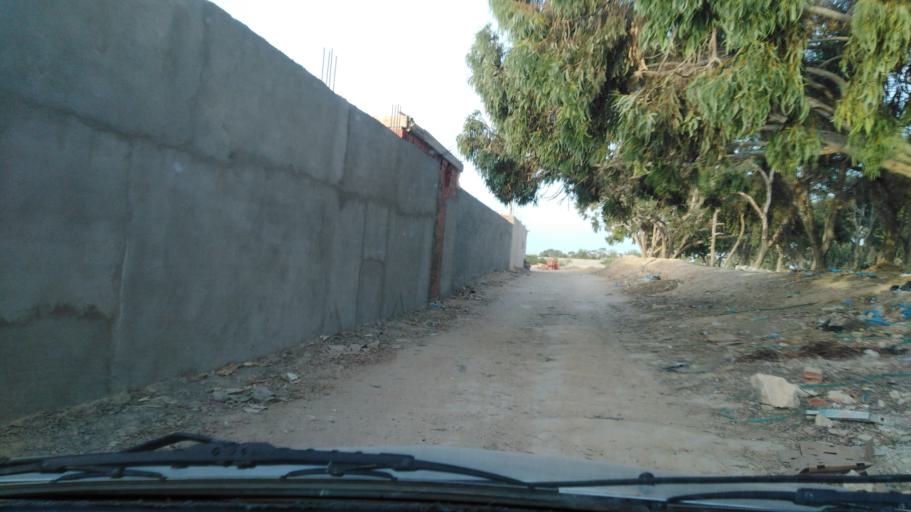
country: TN
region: Qabis
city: Gabes
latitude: 33.9526
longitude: 9.9972
